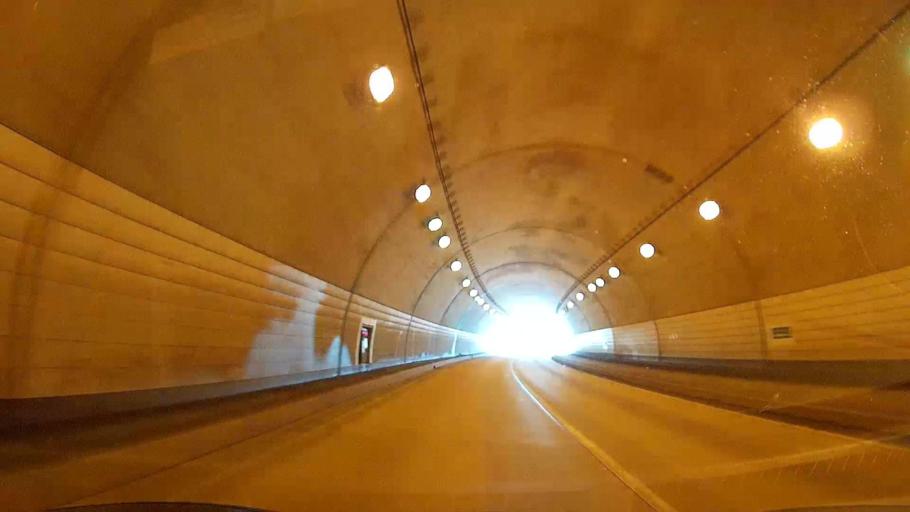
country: JP
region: Niigata
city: Tokamachi
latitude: 37.0034
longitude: 138.6382
